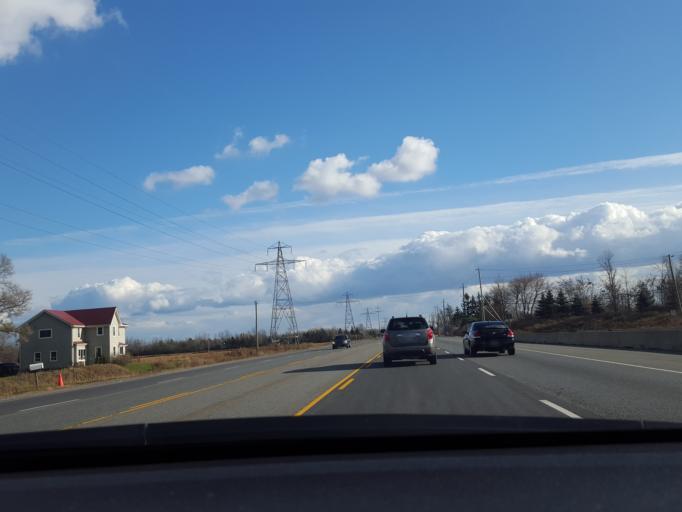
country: CA
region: Ontario
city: Ancaster
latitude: 43.3717
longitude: -79.9990
